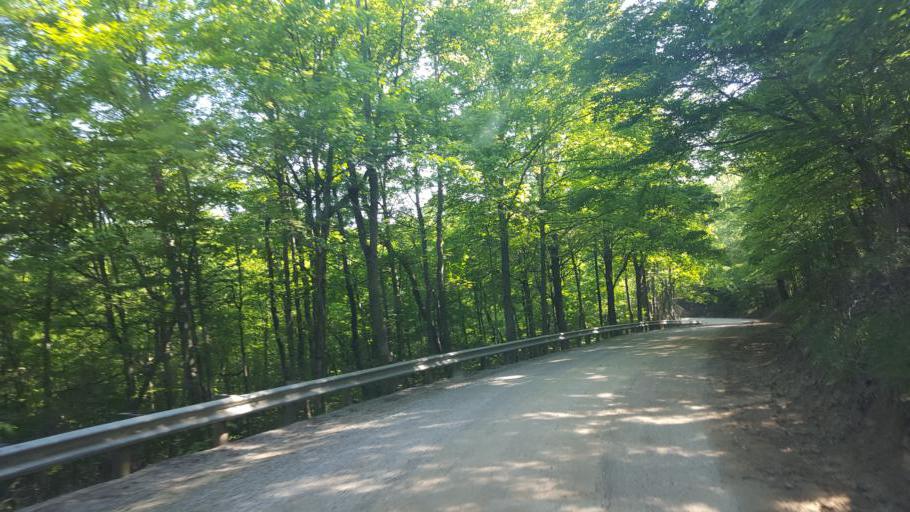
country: US
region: Ohio
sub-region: Jackson County
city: Wellston
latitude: 38.9988
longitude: -82.4320
